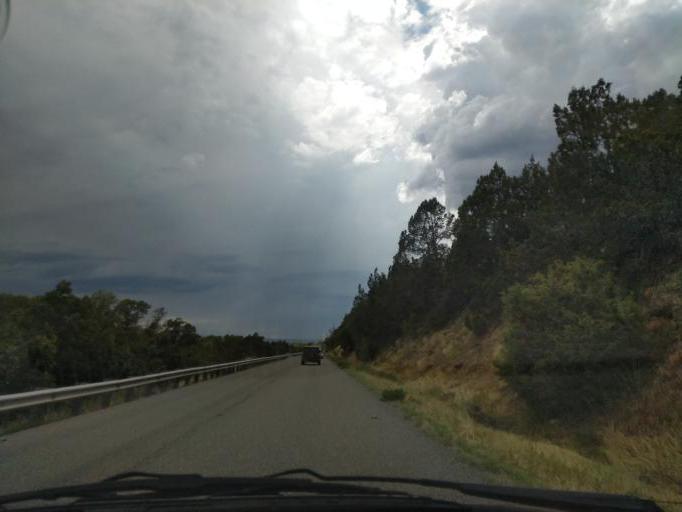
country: US
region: Colorado
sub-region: Delta County
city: Paonia
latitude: 38.8954
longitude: -107.5730
